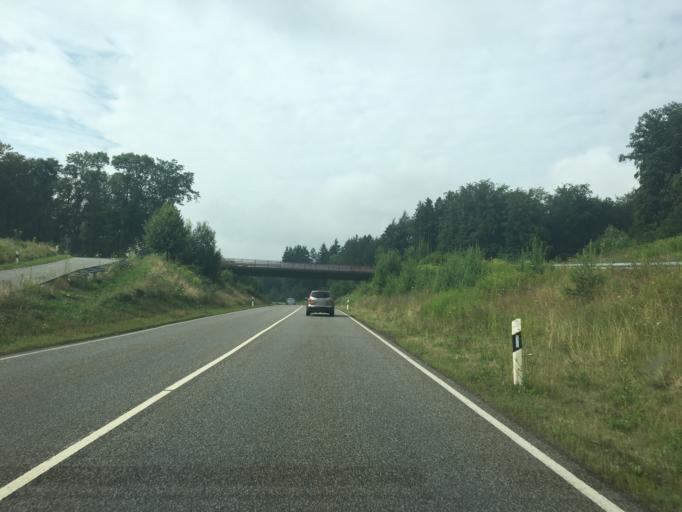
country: DE
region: Rheinland-Pfalz
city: Hillscheid
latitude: 50.3857
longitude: 7.7012
